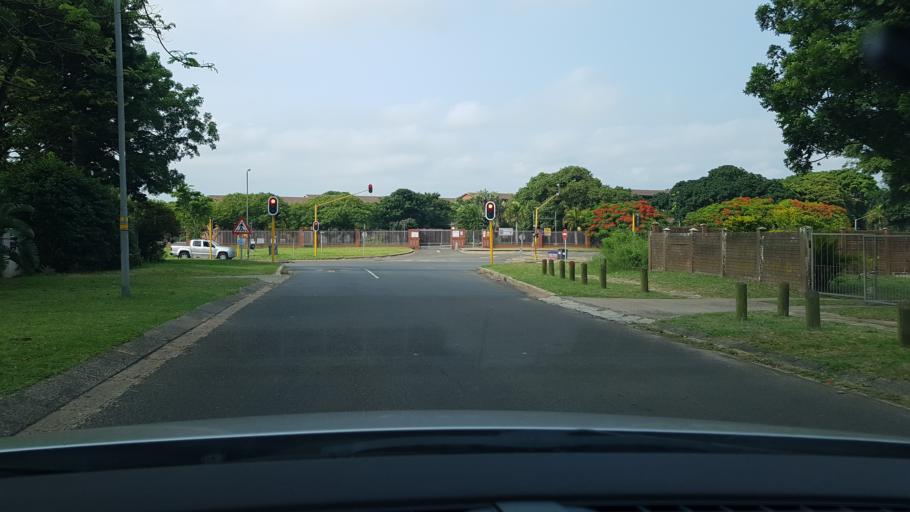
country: ZA
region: KwaZulu-Natal
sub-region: uThungulu District Municipality
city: Richards Bay
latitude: -28.7623
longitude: 32.0551
